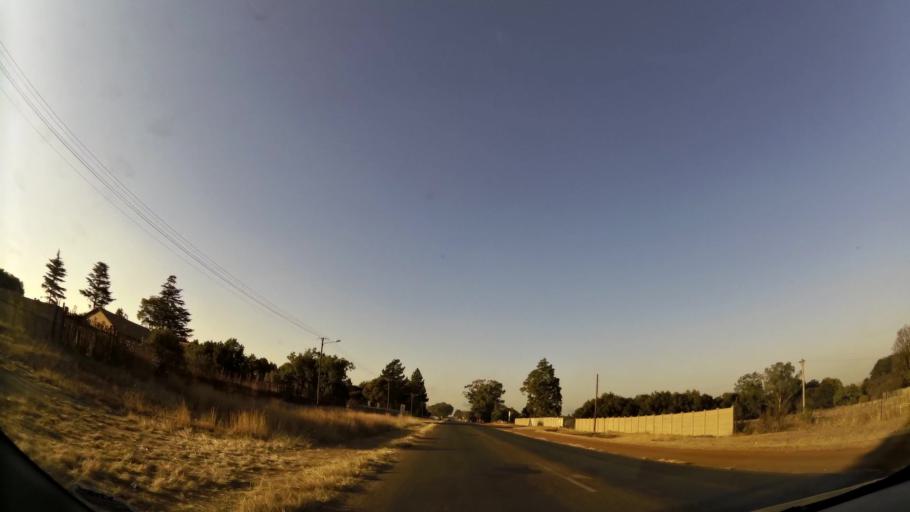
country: ZA
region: Gauteng
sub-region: West Rand District Municipality
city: Randfontein
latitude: -26.2198
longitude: 27.6435
